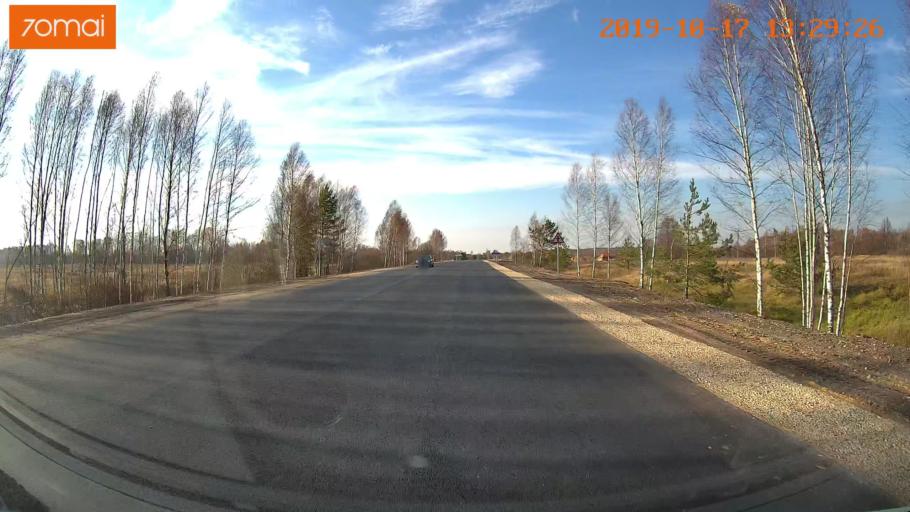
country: RU
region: Vladimir
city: Velikodvorskiy
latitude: 55.1195
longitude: 40.8411
